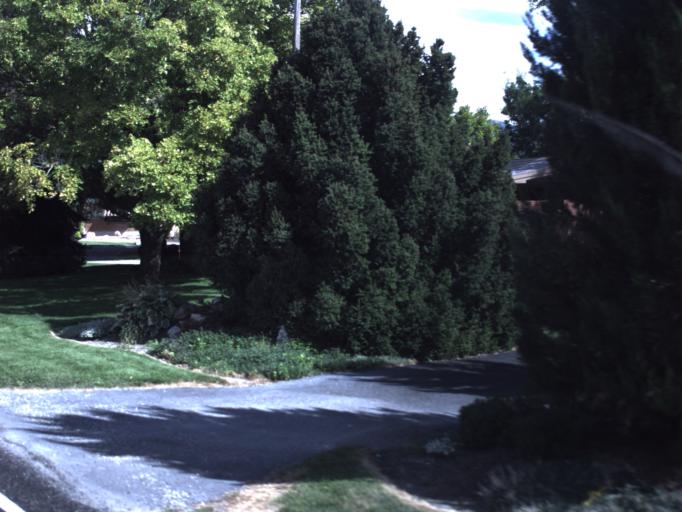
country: US
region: Utah
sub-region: Cache County
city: Richmond
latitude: 41.9228
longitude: -111.8199
